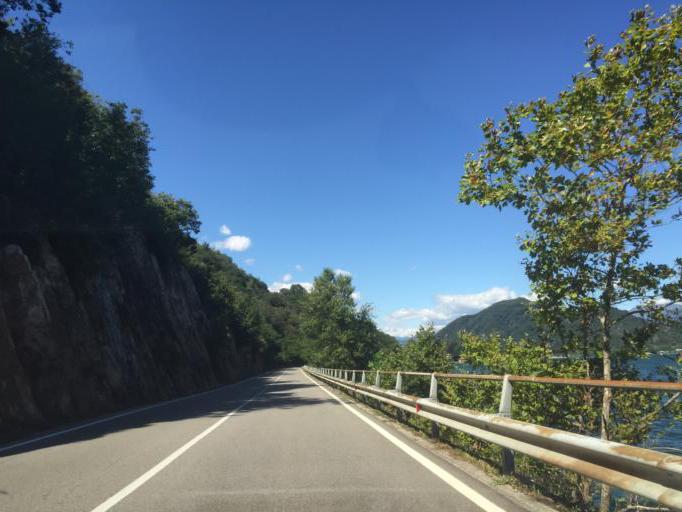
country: IT
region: Lombardy
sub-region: Provincia di Varese
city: Brusimpiano
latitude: 45.9346
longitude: 8.8877
